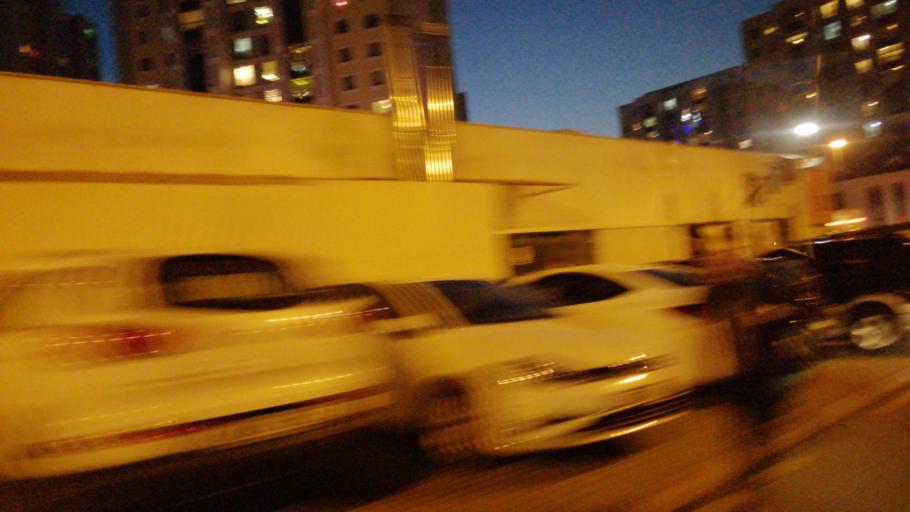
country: TR
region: Istanbul
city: Umraniye
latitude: 40.9996
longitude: 29.1407
